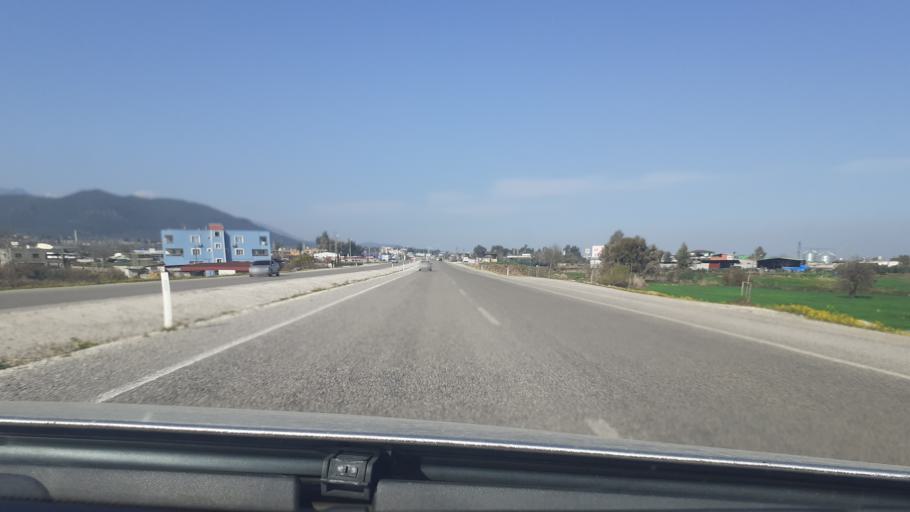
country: TR
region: Hatay
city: Aktepe
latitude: 36.6872
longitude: 36.4721
